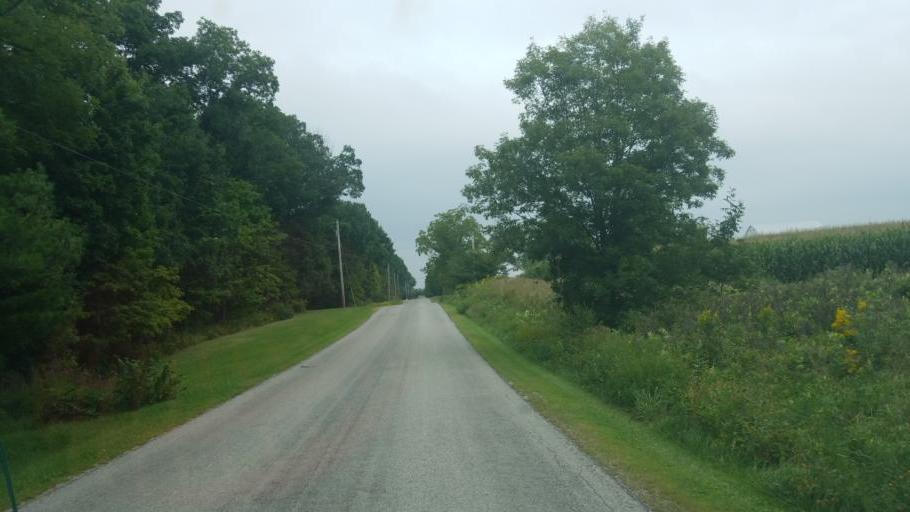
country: US
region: Ohio
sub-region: Medina County
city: Lodi
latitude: 40.9597
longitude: -81.9856
